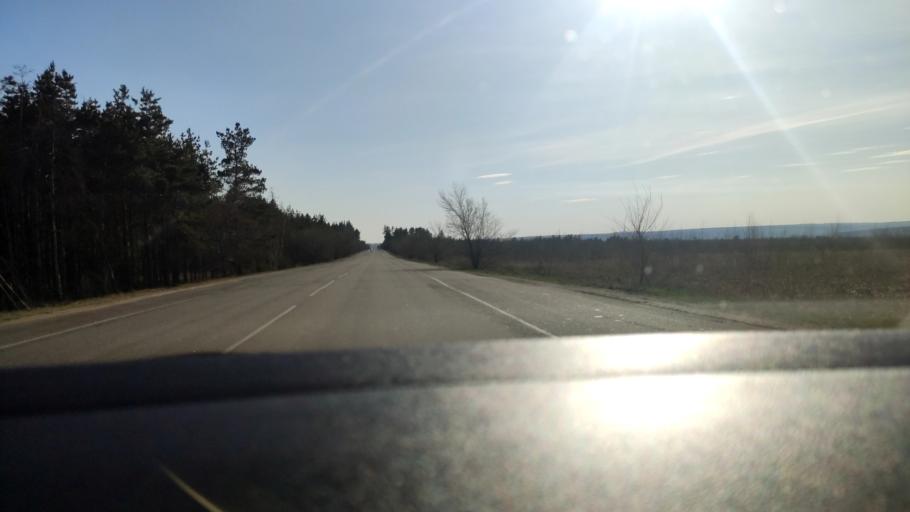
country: RU
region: Voronezj
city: Kolodeznyy
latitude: 51.3691
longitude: 39.2022
